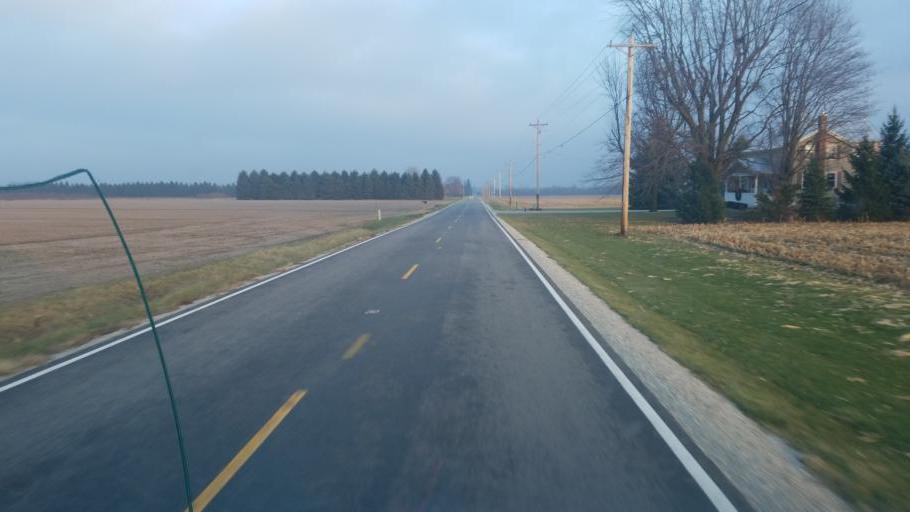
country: US
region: Ohio
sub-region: Wyandot County
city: Carey
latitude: 40.9998
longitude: -83.3001
